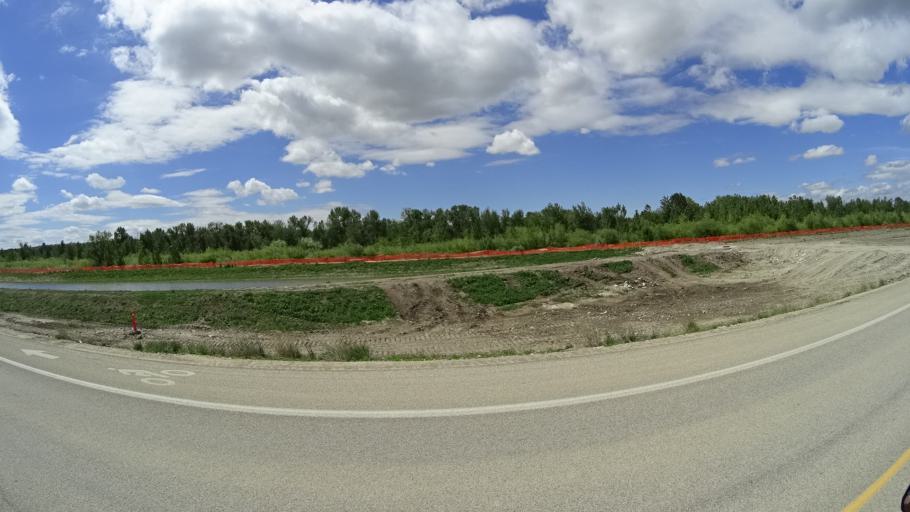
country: US
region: Idaho
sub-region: Ada County
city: Boise
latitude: 43.5715
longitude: -116.1351
